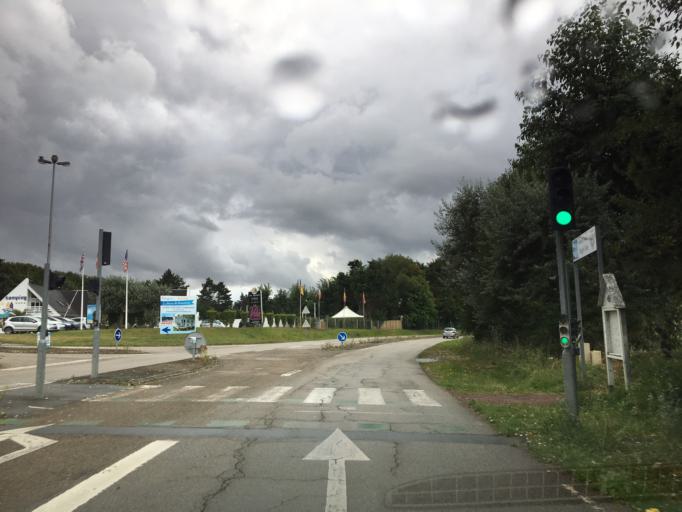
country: FR
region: Lower Normandy
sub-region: Departement du Calvados
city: Bernieres-sur-Mer
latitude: 49.3330
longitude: -0.4279
